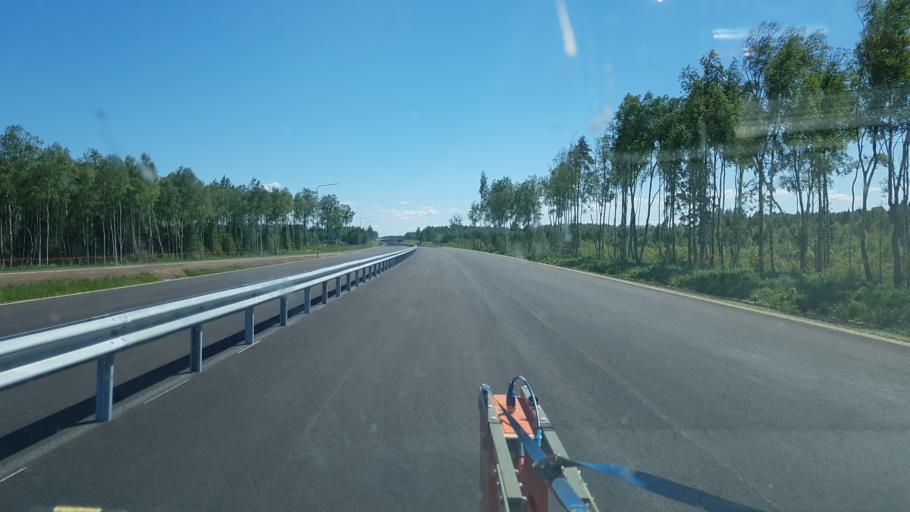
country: EE
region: Harju
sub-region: Anija vald
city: Kehra
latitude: 59.0778
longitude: 25.3372
